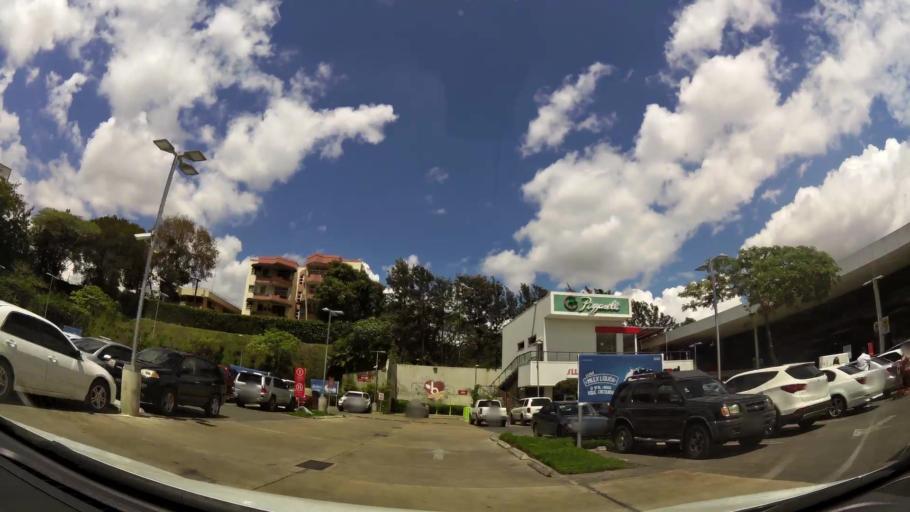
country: DO
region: Santiago
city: Santiago de los Caballeros
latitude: 19.4535
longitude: -70.6862
